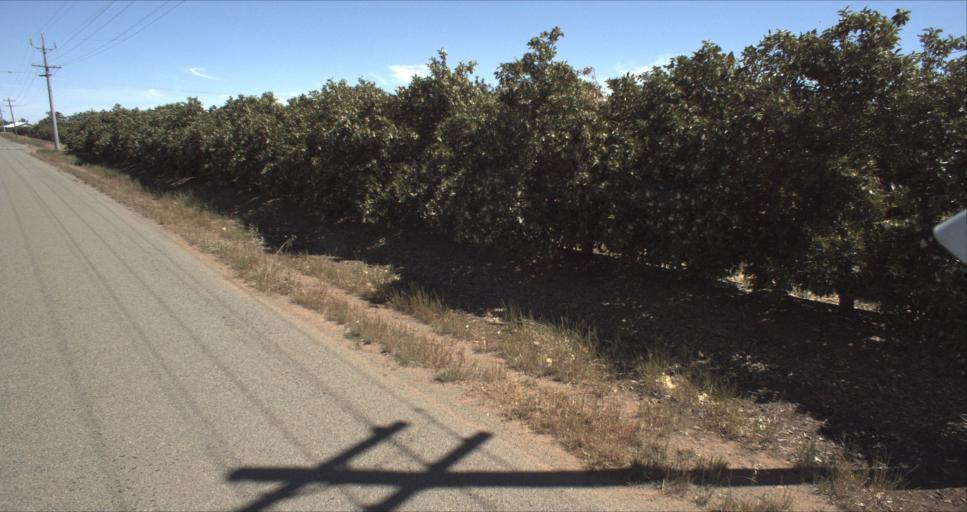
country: AU
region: New South Wales
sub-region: Leeton
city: Leeton
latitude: -34.5358
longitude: 146.3524
